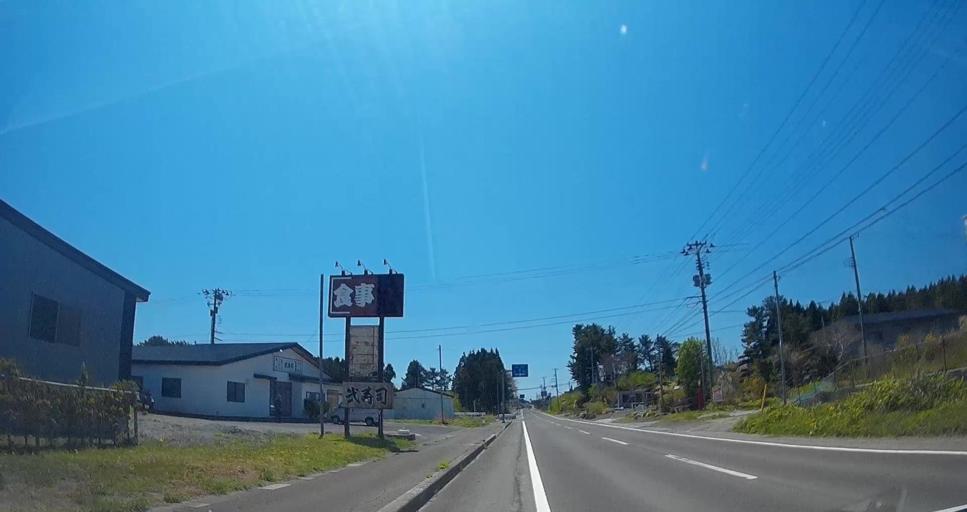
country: JP
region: Aomori
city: Mutsu
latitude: 41.0806
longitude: 141.3858
